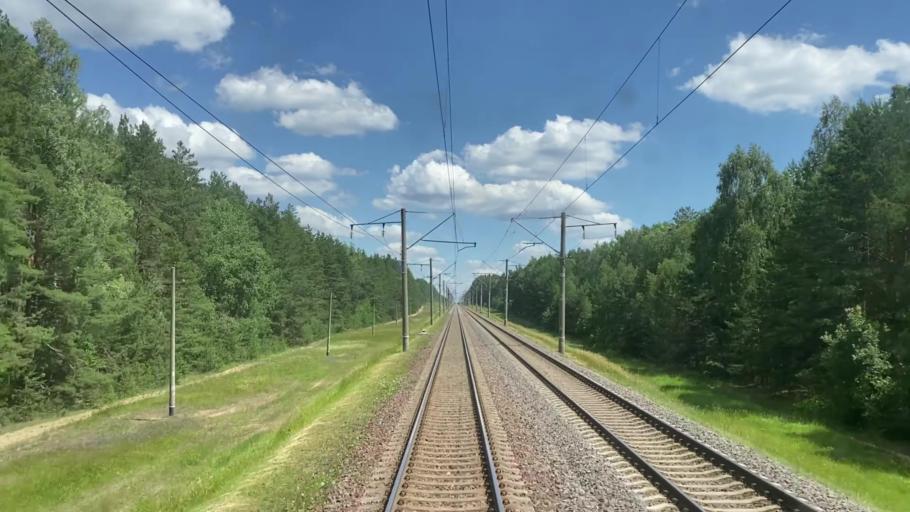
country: BY
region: Brest
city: Ivatsevichy
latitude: 52.8553
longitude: 25.5781
